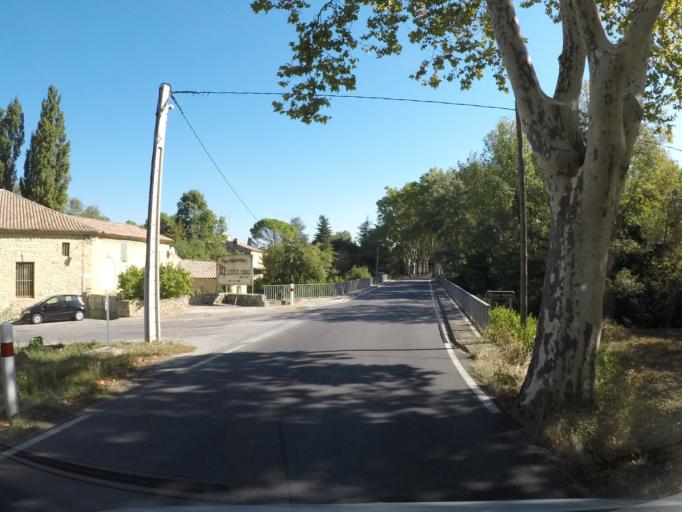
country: FR
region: Languedoc-Roussillon
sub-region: Departement du Gard
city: Montaren-et-Saint-Mediers
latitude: 44.0015
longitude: 4.3863
